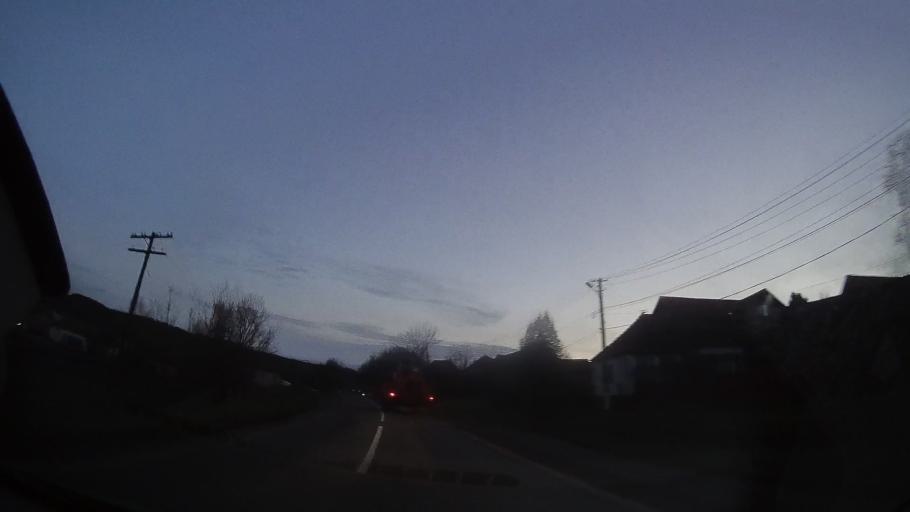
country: RO
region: Mures
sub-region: Comuna Sarmasu
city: Sarmasu
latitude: 46.7815
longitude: 24.2026
